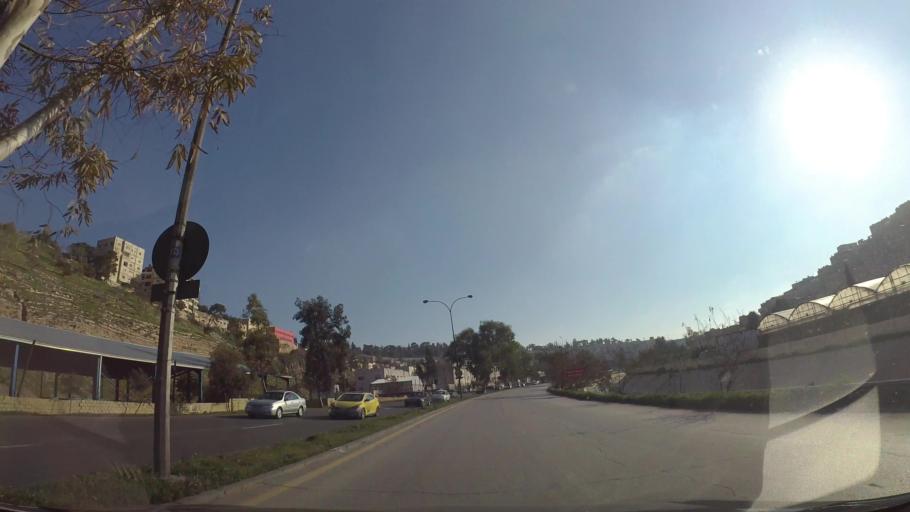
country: JO
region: Amman
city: Amman
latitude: 31.9737
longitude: 35.9717
